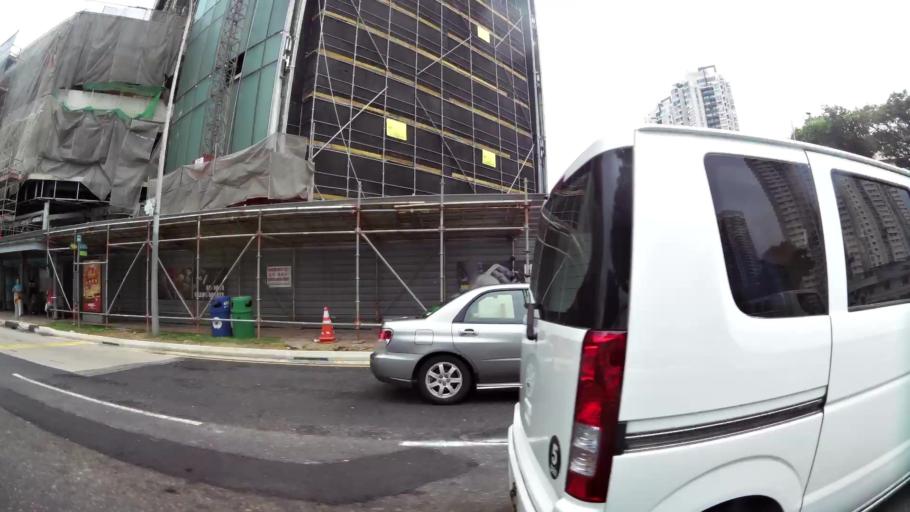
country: SG
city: Singapore
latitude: 1.3136
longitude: 103.8605
